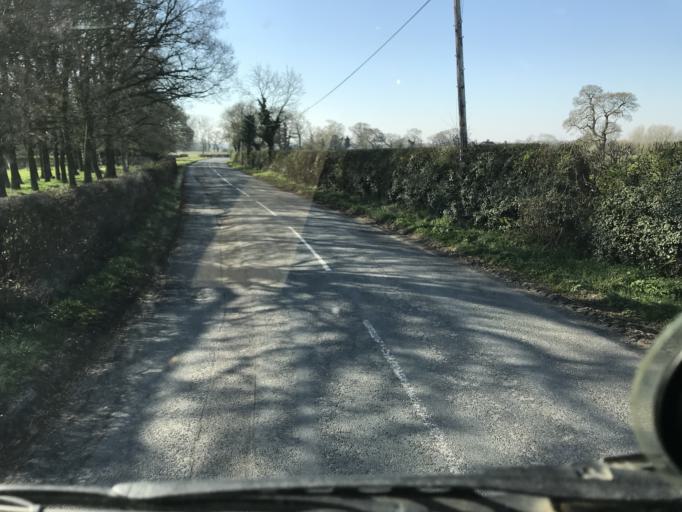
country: GB
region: England
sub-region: Cheshire West and Chester
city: Aldford
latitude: 53.1387
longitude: -2.8430
